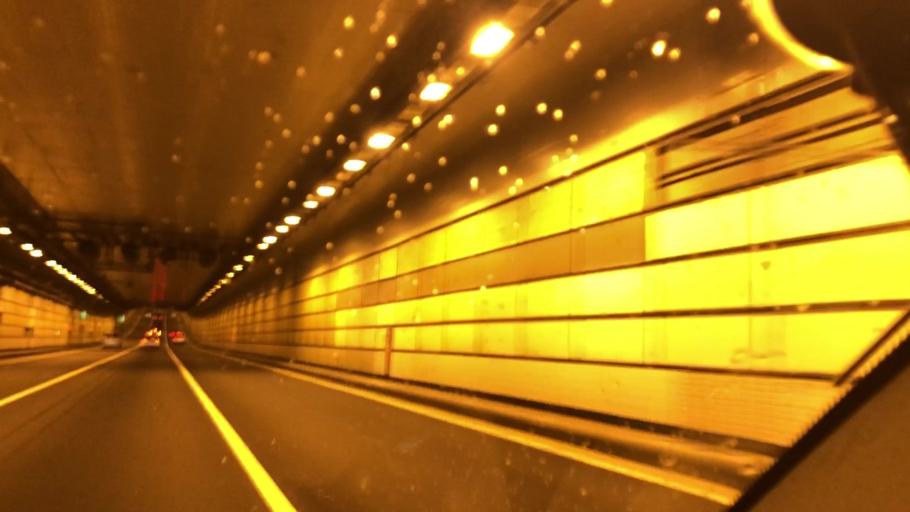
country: JP
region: Kanagawa
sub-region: Kawasaki-shi
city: Kawasaki
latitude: 35.5662
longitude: 139.7653
